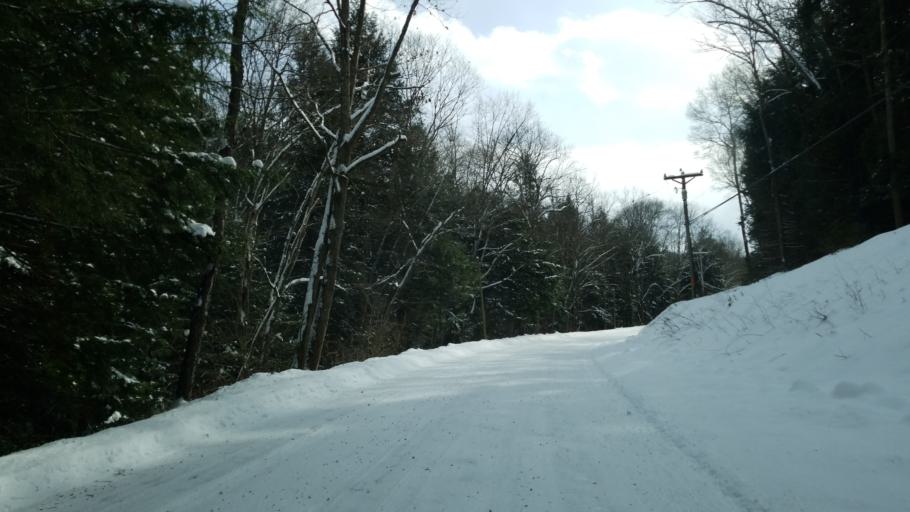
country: US
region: Pennsylvania
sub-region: Clearfield County
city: Clearfield
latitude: 41.0511
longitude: -78.4664
